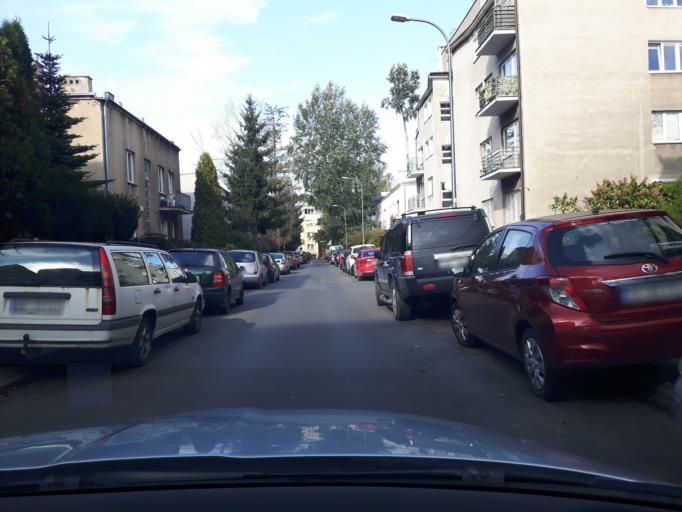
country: PL
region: Masovian Voivodeship
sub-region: Warszawa
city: Praga Poludnie
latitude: 52.2377
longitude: 21.0626
